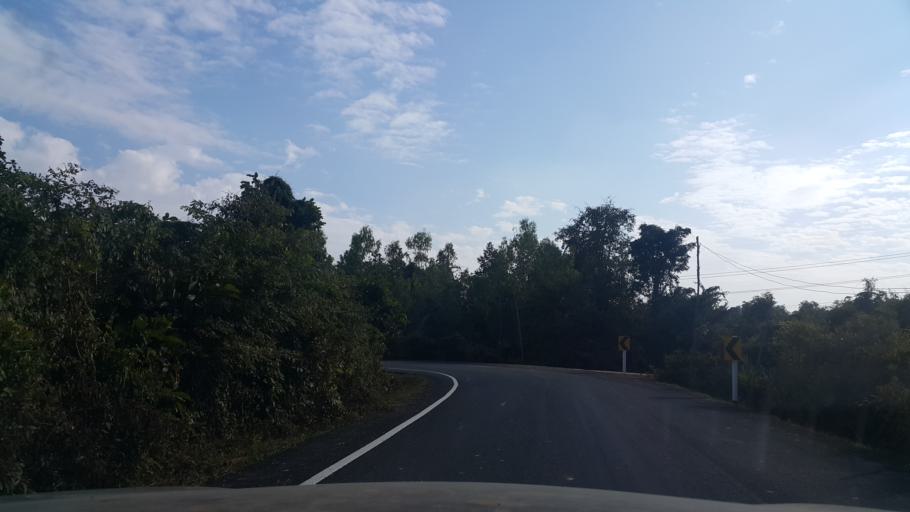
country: TH
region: Lampang
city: Hang Chat
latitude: 18.2915
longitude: 99.3599
